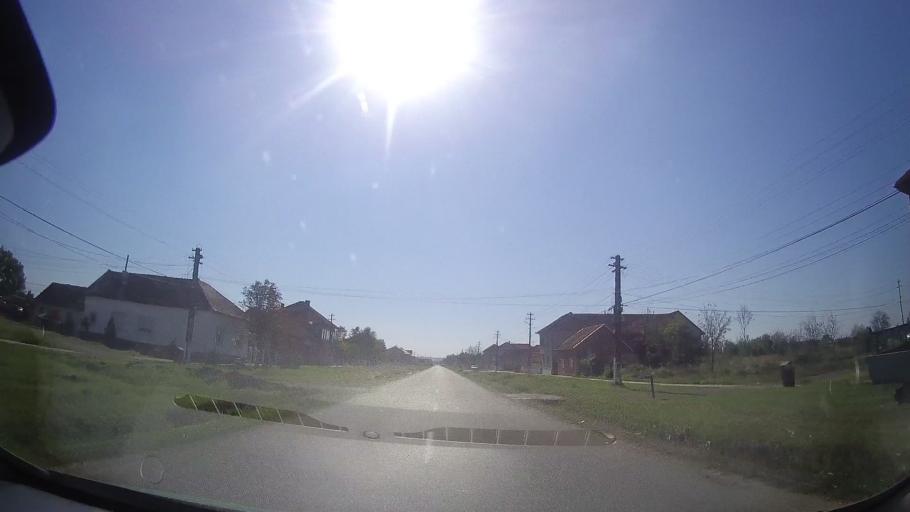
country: RO
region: Timis
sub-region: Comuna Bethausen
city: Bethausen
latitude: 45.8351
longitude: 21.9596
